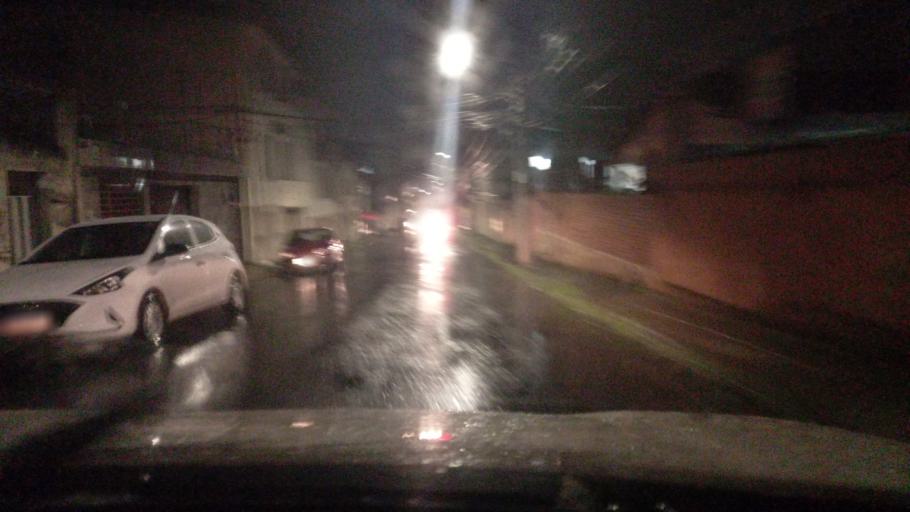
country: BR
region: Minas Gerais
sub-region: Belo Horizonte
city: Belo Horizonte
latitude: -19.9107
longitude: -43.9133
